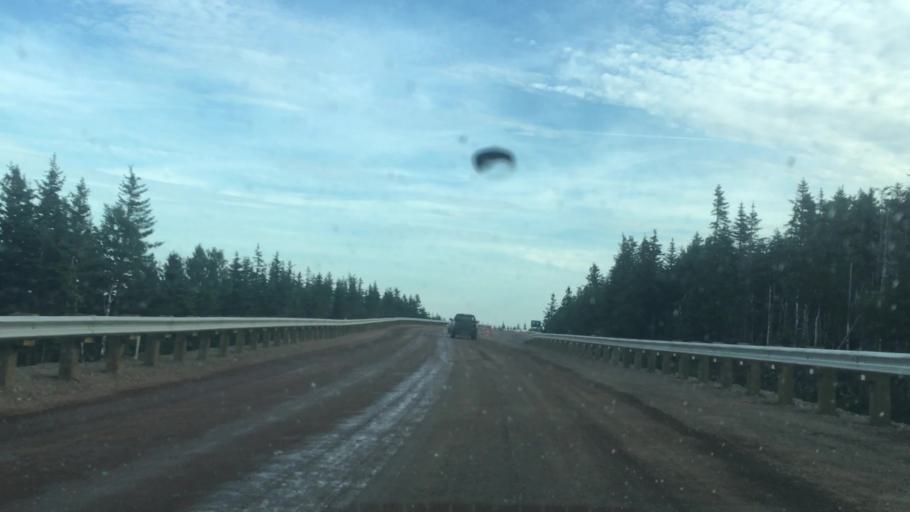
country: CA
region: Nova Scotia
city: Sydney Mines
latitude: 46.8054
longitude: -60.8442
